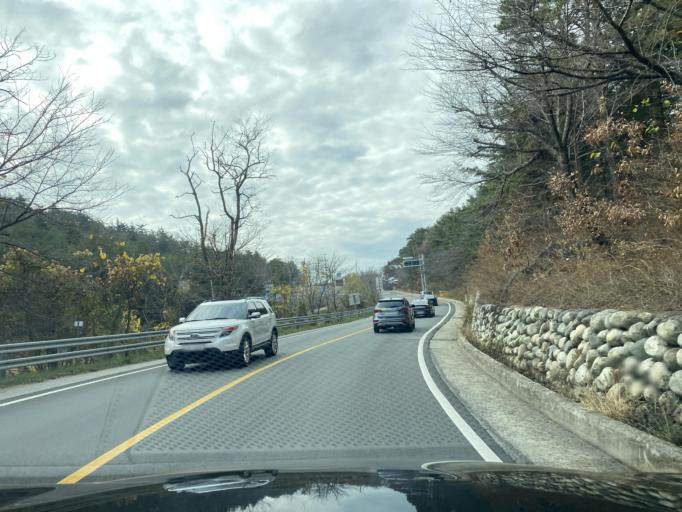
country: KR
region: Chungcheongnam-do
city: Hongsung
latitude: 36.6630
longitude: 126.6331
